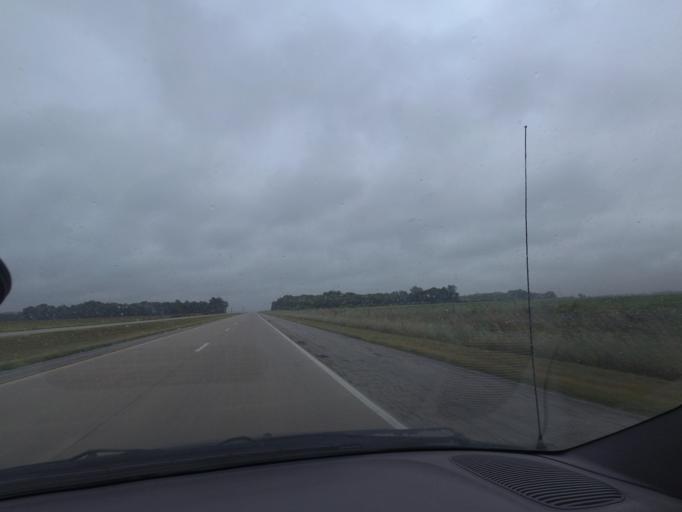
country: US
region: Illinois
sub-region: Adams County
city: Payson
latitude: 39.7387
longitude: -91.2543
